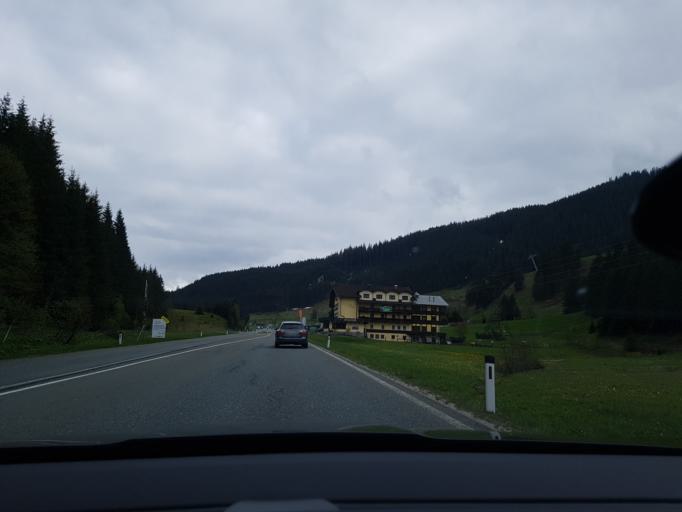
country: AT
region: Salzburg
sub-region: Politischer Bezirk Zell am See
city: Hollersbach im Pinzgau
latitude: 47.3149
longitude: 12.4061
